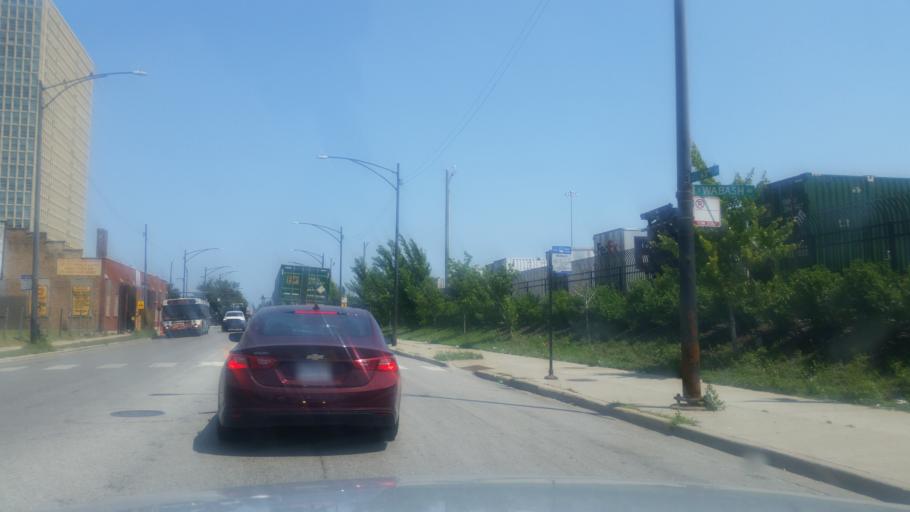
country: US
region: Illinois
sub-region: Cook County
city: Chicago
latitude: 41.7800
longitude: -87.6238
